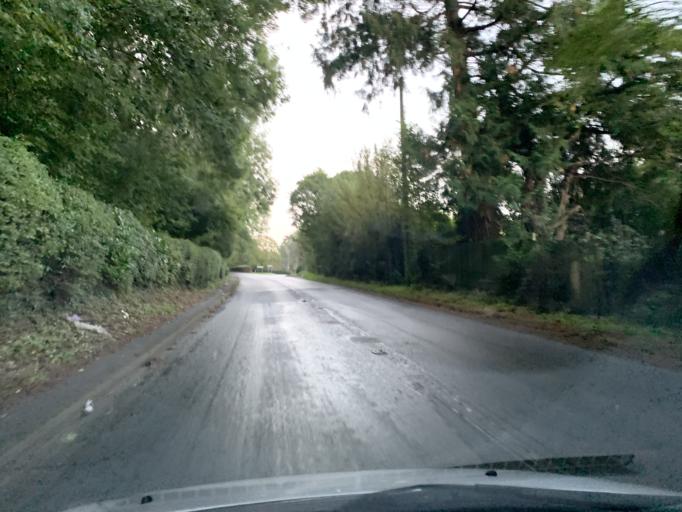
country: GB
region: England
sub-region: Wiltshire
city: Alderbury
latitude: 51.0534
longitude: -1.7550
